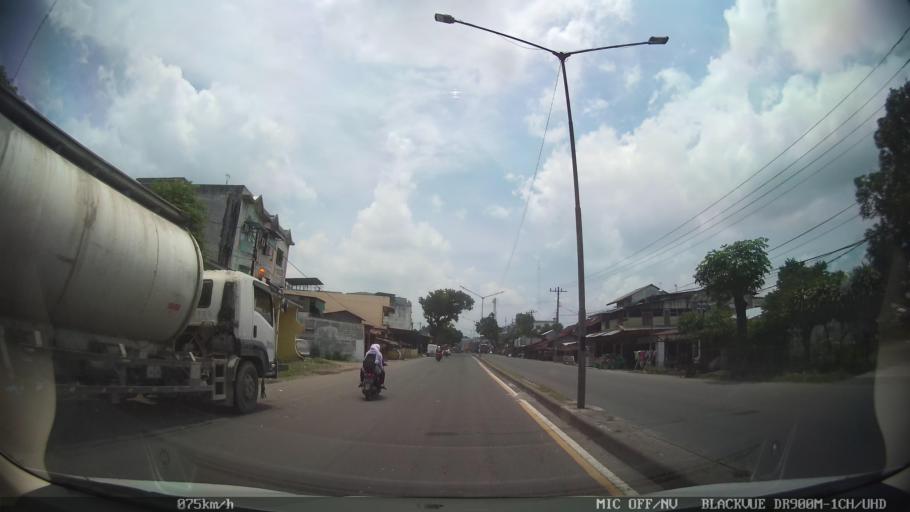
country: ID
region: North Sumatra
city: Labuhan Deli
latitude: 3.6994
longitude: 98.6754
